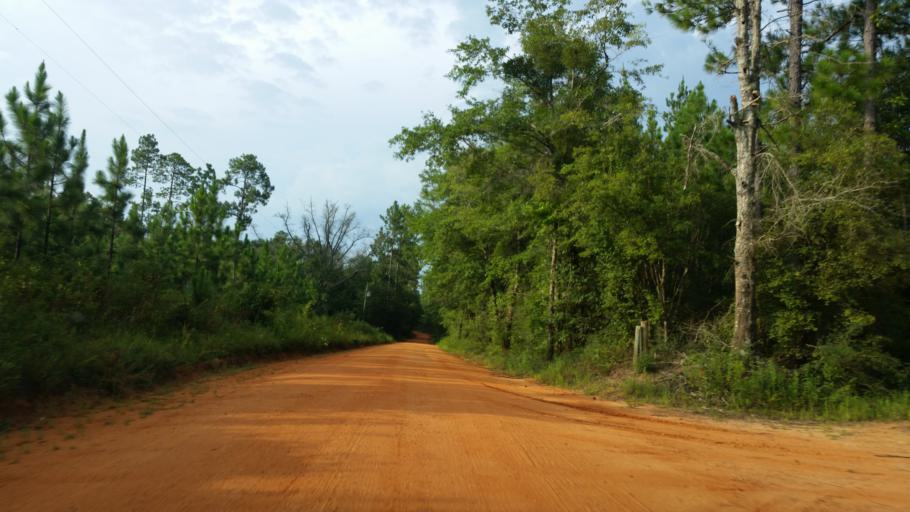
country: US
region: Alabama
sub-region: Escambia County
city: Atmore
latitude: 30.8940
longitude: -87.5834
